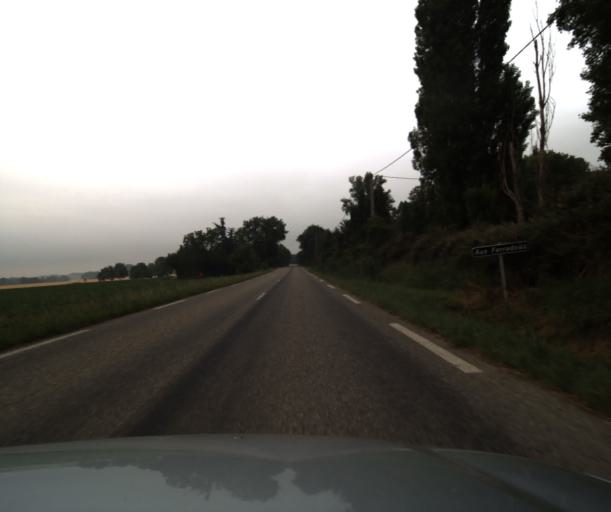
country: FR
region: Midi-Pyrenees
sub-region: Departement du Tarn-et-Garonne
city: Beaumont-de-Lomagne
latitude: 43.7832
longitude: 0.8900
